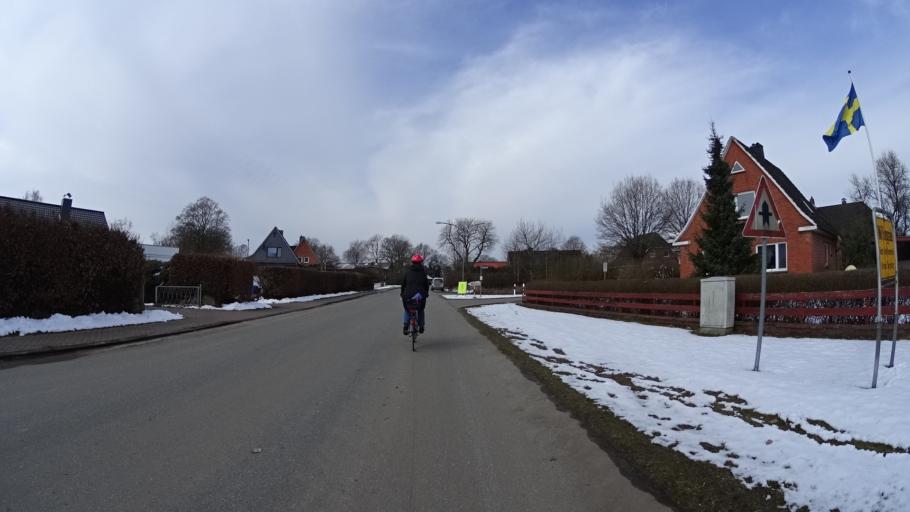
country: DE
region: Schleswig-Holstein
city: Gross Kummerfeld
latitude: 54.0281
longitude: 10.1203
